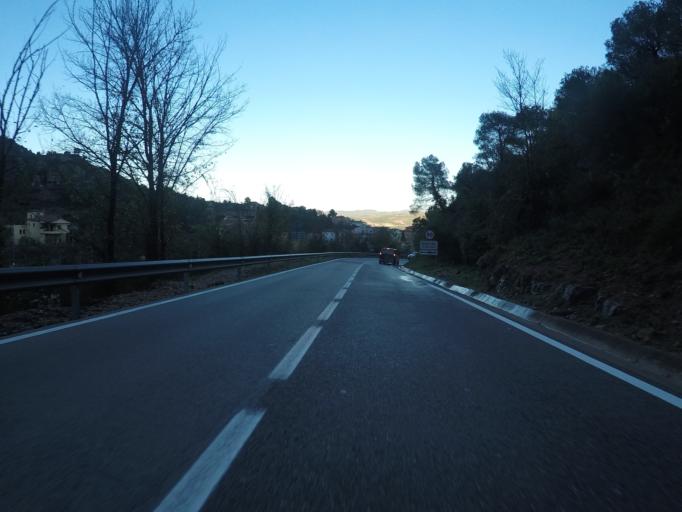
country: ES
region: Catalonia
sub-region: Provincia de Barcelona
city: Monistrol de Montserrat
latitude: 41.6089
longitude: 1.8394
